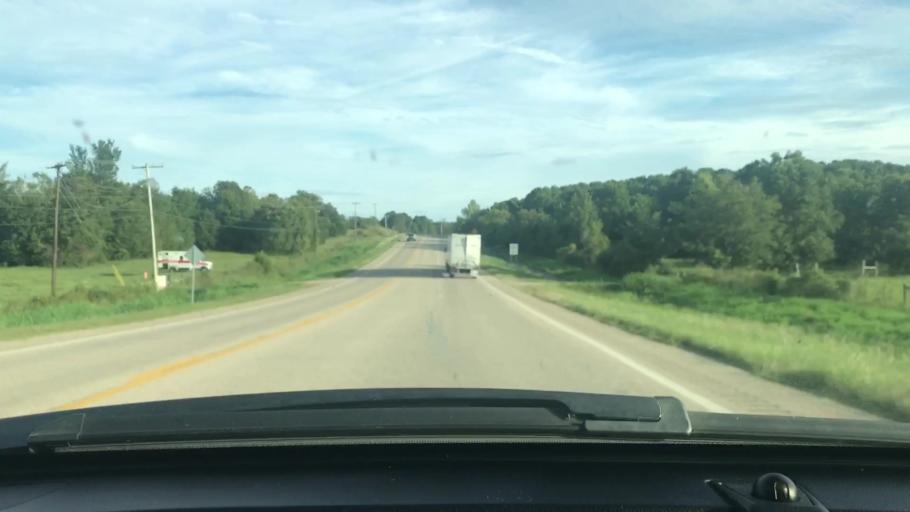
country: US
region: Arkansas
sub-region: Randolph County
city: Pocahontas
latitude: 36.1921
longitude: -91.1655
